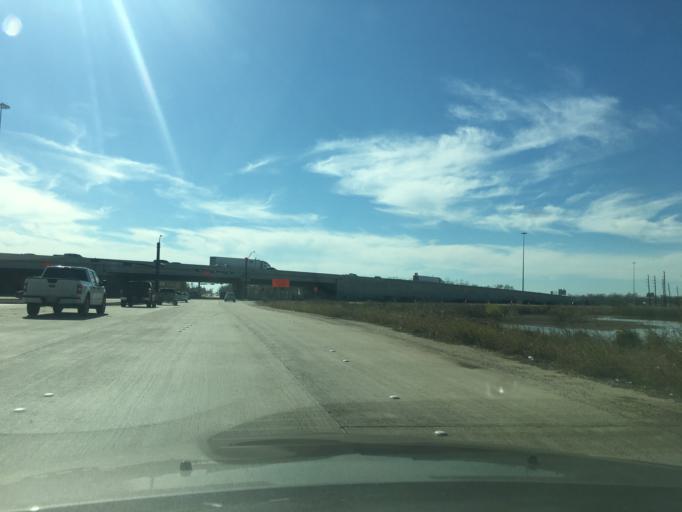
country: US
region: Texas
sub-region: Fort Bend County
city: Greatwood
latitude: 29.5575
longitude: -95.7164
